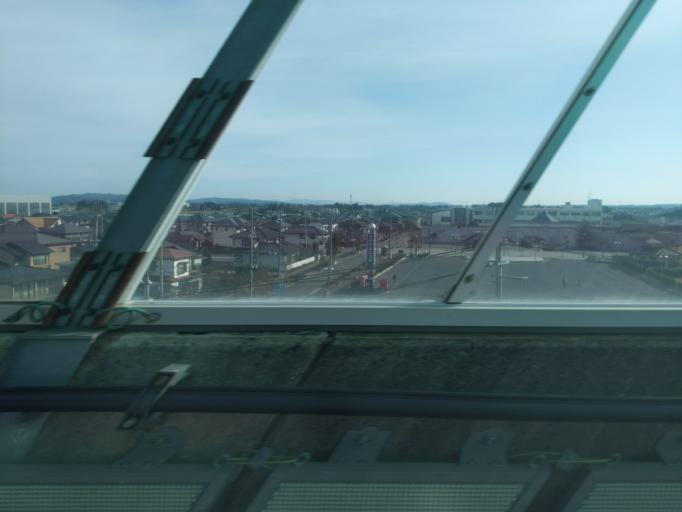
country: JP
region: Miyagi
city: Furukawa
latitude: 38.5829
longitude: 140.9711
